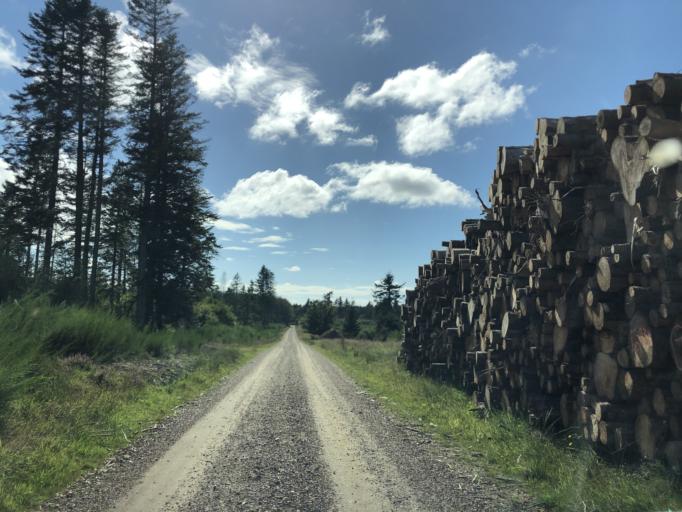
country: DK
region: Central Jutland
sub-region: Holstebro Kommune
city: Ulfborg
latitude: 56.2368
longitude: 8.4924
